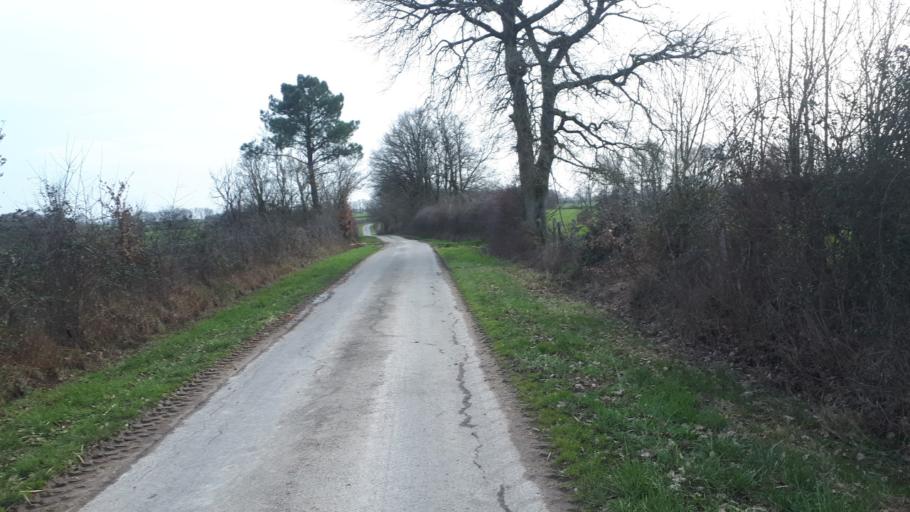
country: FR
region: Poitou-Charentes
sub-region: Departement de la Vienne
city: Archigny
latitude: 46.6257
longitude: 0.7456
